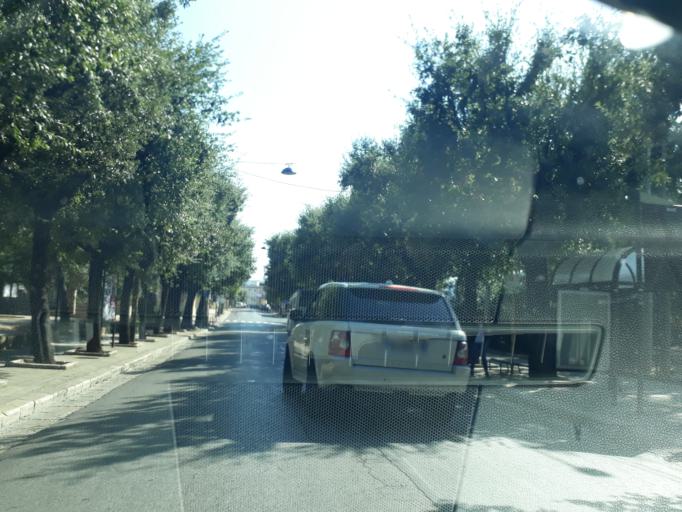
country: IT
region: Apulia
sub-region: Provincia di Brindisi
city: Fasano
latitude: 40.8332
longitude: 17.3595
